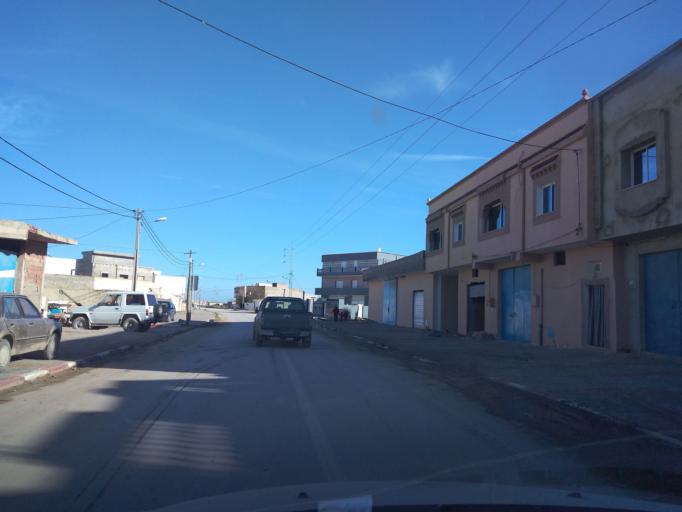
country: TN
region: Ariana
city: Qal'at al Andalus
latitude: 37.0606
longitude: 10.1279
